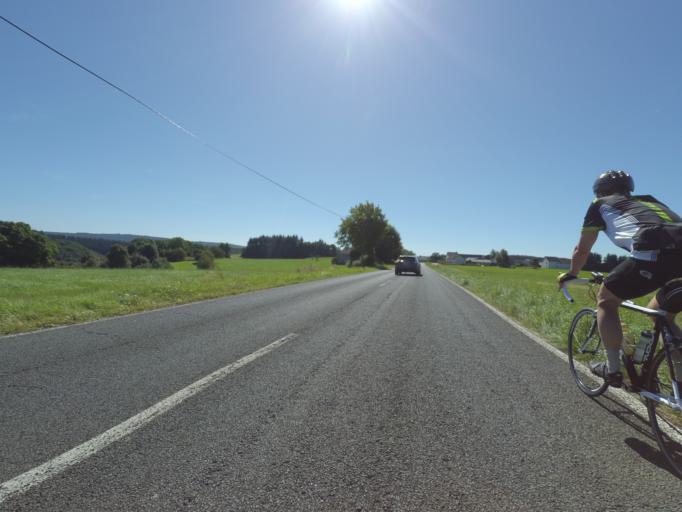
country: DE
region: Rheinland-Pfalz
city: Schladt
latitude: 50.0372
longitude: 6.8402
